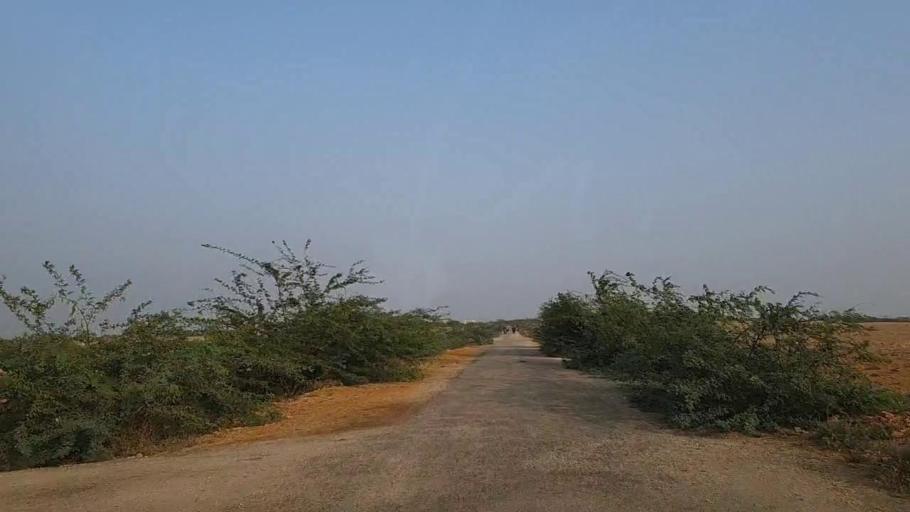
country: PK
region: Sindh
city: Thatta
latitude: 24.6903
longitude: 67.8228
